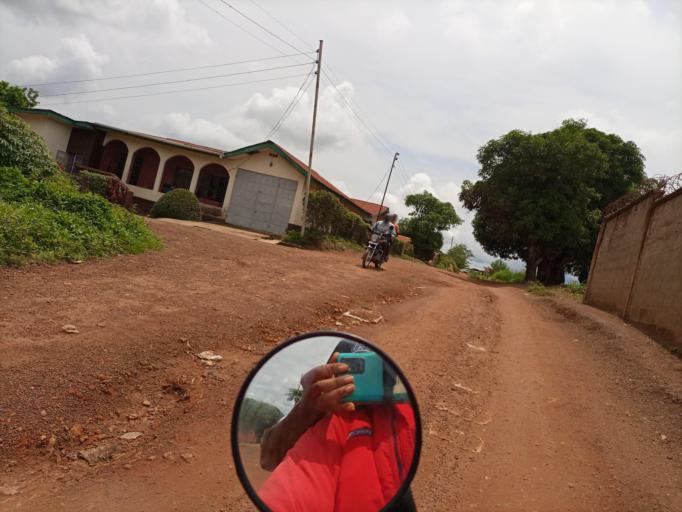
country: SL
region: Southern Province
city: Bo
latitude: 7.9708
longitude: -11.7212
